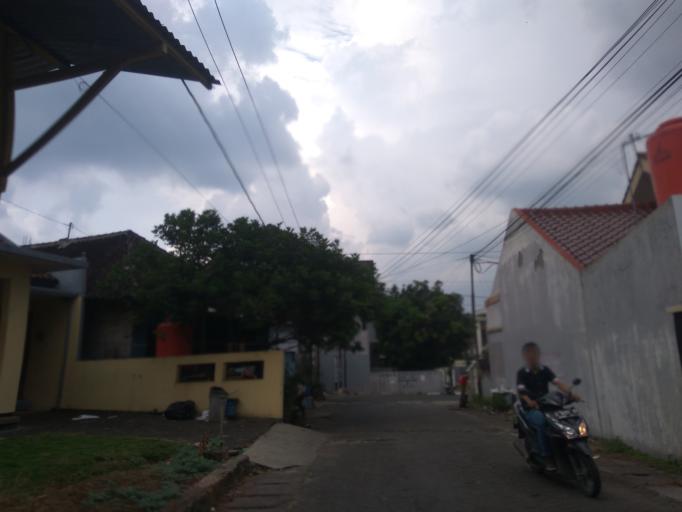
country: ID
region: Central Java
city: Semarang
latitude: -7.0646
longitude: 110.4442
